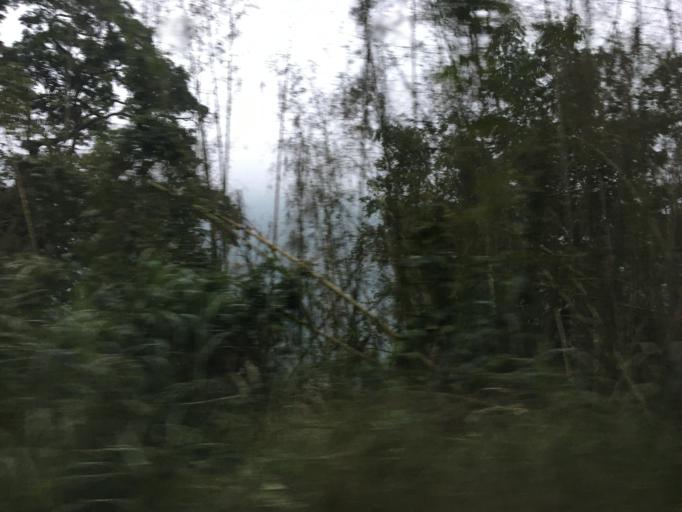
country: TW
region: Taiwan
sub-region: Chiayi
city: Jiayi Shi
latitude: 23.5149
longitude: 120.6575
